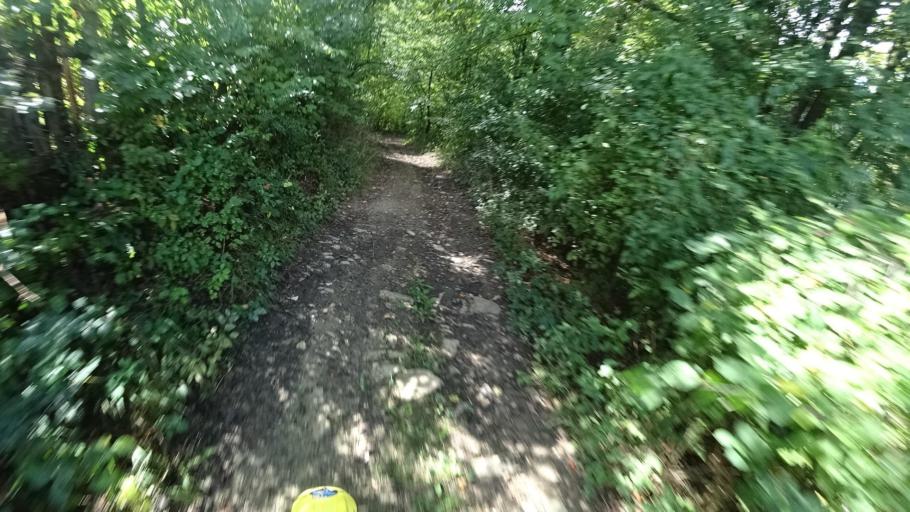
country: BA
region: Republika Srpska
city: Hiseti
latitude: 44.7606
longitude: 17.1581
